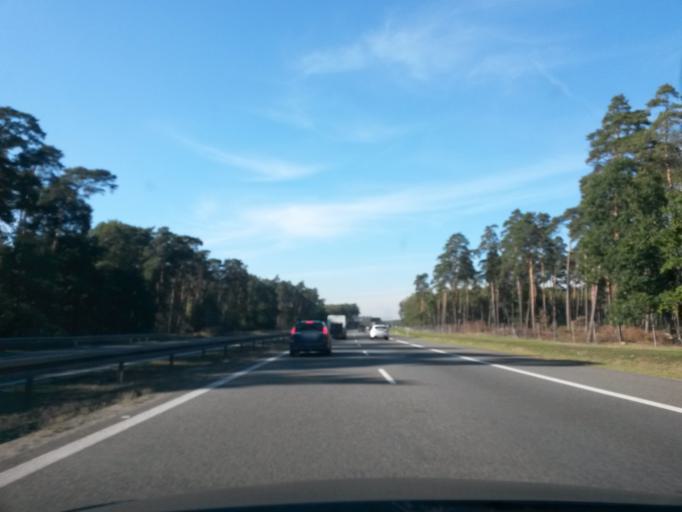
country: PL
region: Opole Voivodeship
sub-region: Powiat opolski
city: Proszkow
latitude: 50.5362
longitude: 17.9047
